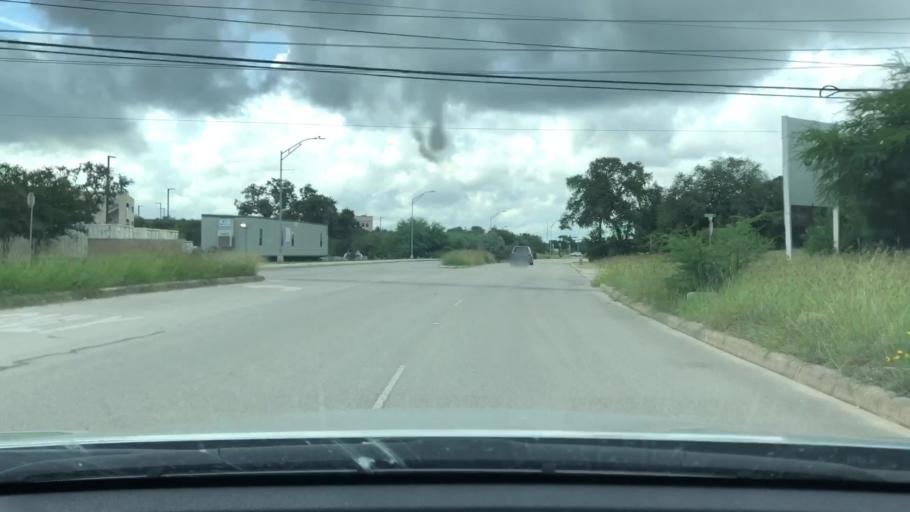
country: US
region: Texas
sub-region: Bexar County
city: Hollywood Park
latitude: 29.6172
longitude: -98.4766
